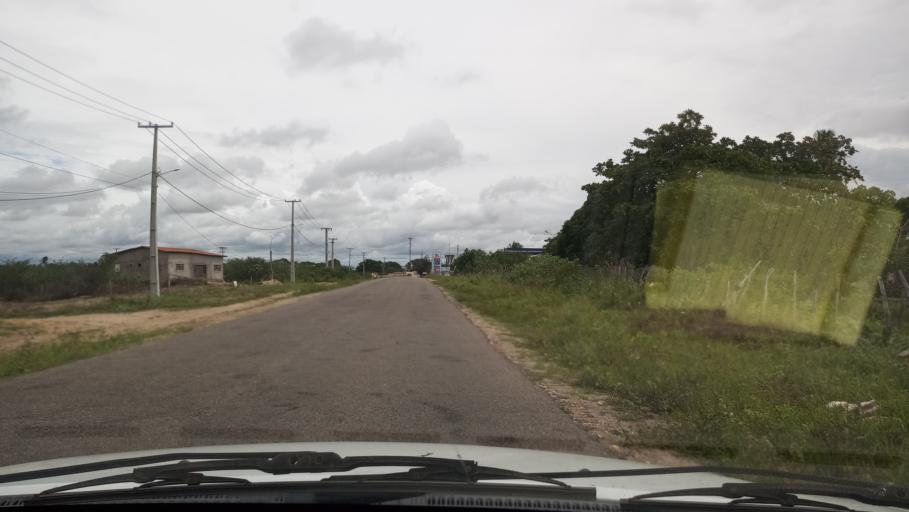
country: BR
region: Rio Grande do Norte
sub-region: Poco Branco
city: Poco Branco
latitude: -5.6166
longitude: -35.6520
